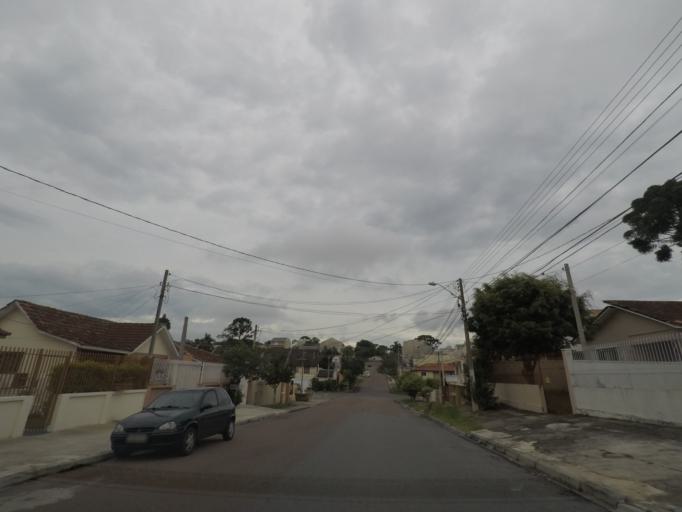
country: BR
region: Parana
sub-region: Curitiba
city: Curitiba
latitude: -25.4683
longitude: -49.3041
